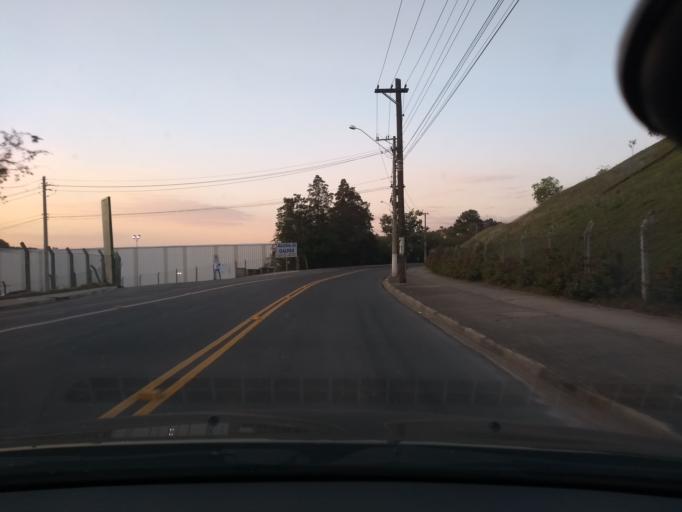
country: BR
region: Sao Paulo
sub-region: Itupeva
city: Itupeva
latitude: -23.1434
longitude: -47.0430
